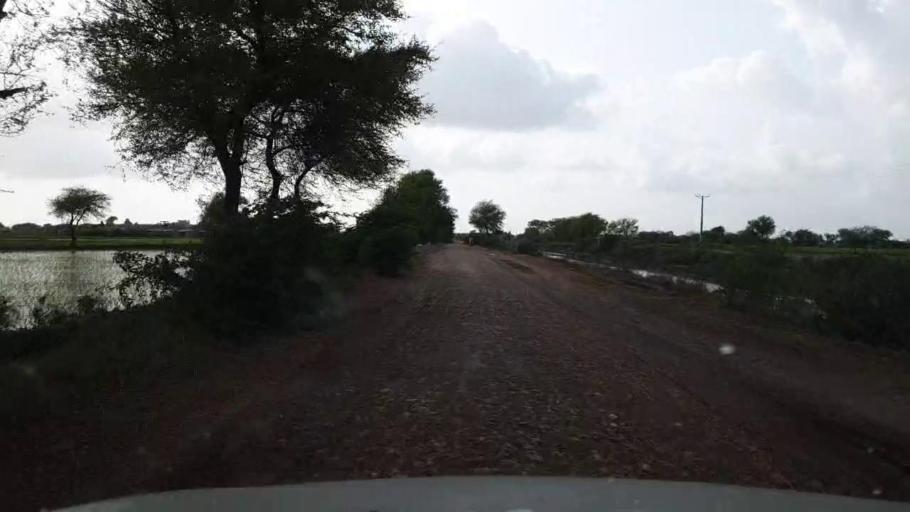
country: PK
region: Sindh
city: Kario
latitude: 24.7704
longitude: 68.5967
